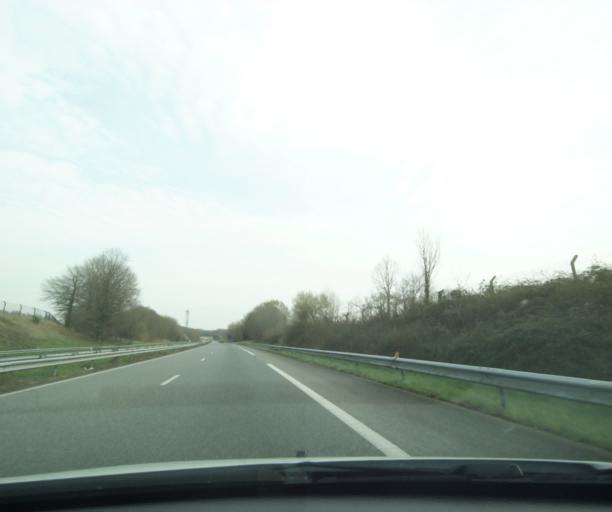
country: FR
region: Aquitaine
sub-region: Departement des Pyrenees-Atlantiques
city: Orthez
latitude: 43.4794
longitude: -0.8028
